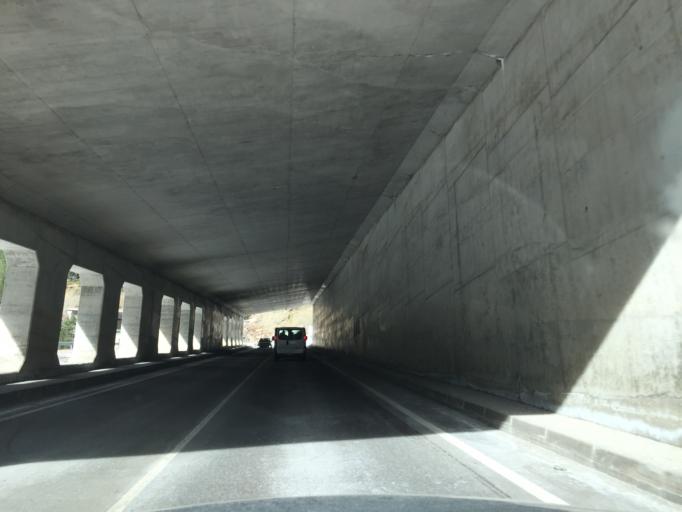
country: ES
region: Aragon
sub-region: Provincia de Huesca
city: Bielsa
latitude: 42.7119
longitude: 0.2042
